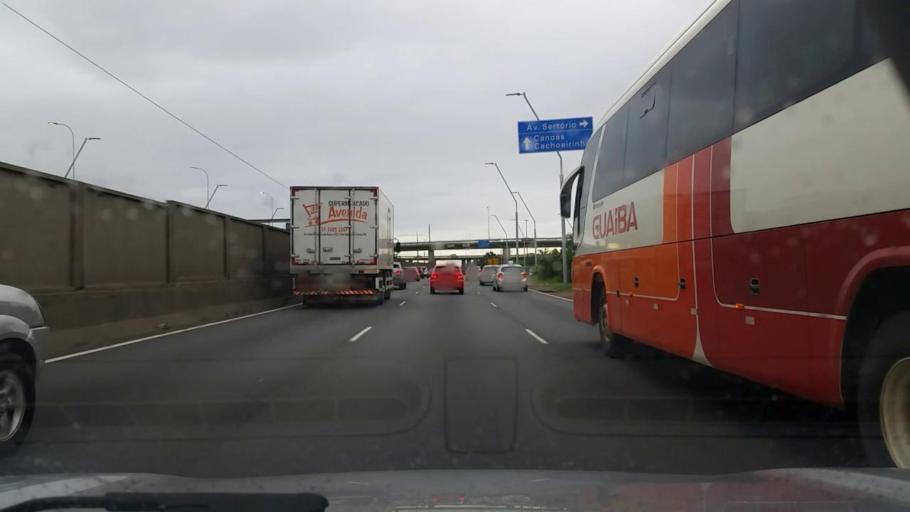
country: BR
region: Rio Grande do Sul
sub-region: Porto Alegre
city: Porto Alegre
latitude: -30.0006
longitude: -51.2073
